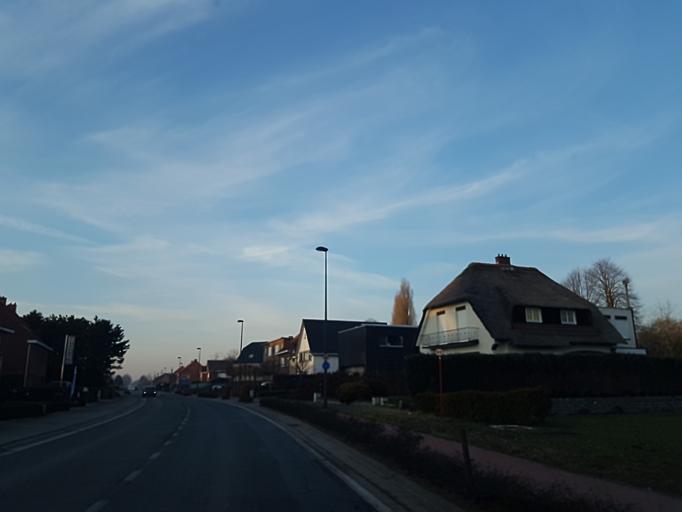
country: BE
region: Flanders
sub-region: Provincie Antwerpen
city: Oostmalle
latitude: 51.3043
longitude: 4.7293
